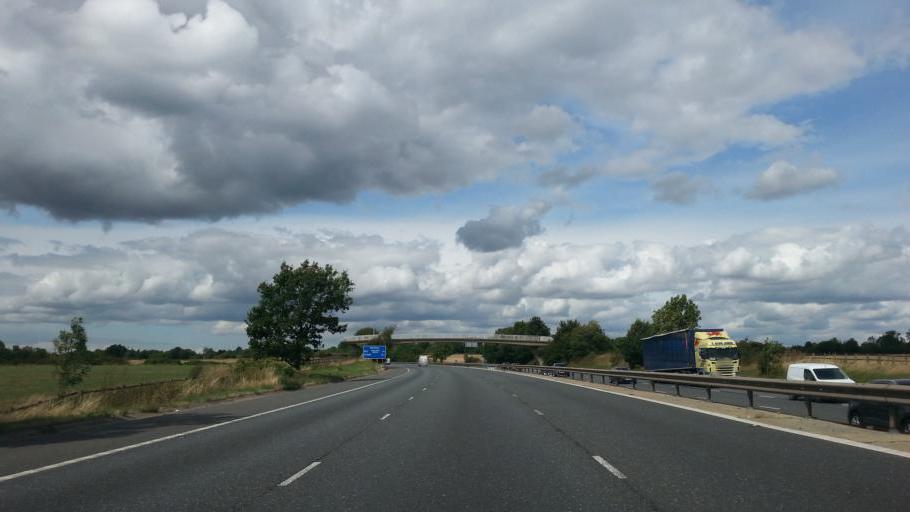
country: GB
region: England
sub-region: Essex
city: Little Hallingbury
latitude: 51.8390
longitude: 0.1928
